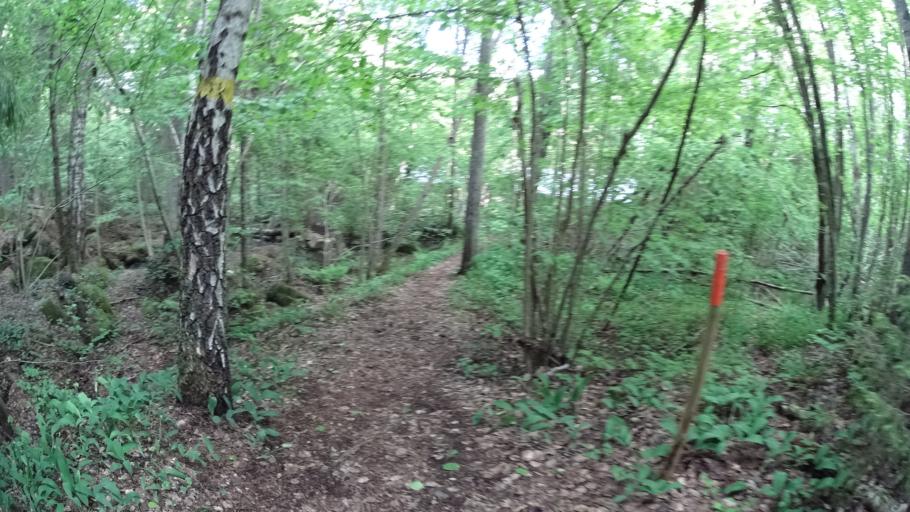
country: FI
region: Uusimaa
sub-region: Raaseporin
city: Pohja
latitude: 60.1453
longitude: 23.5411
